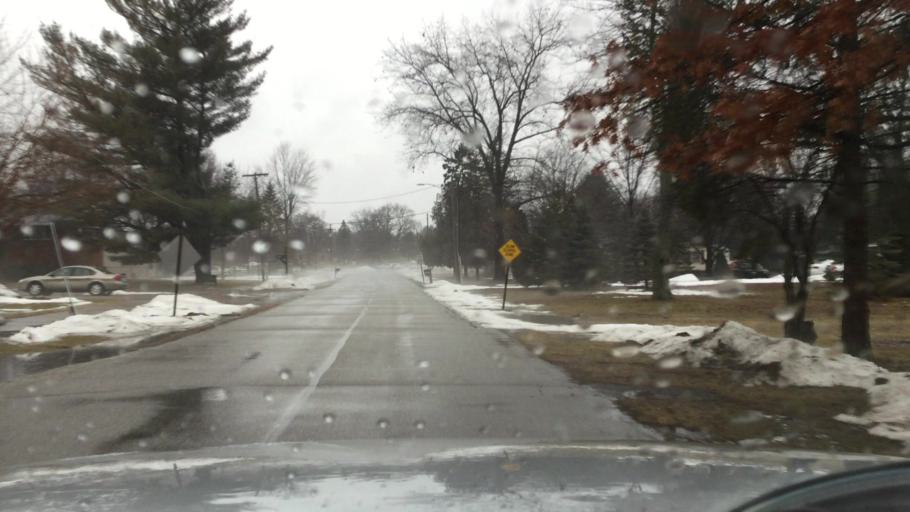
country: US
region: Michigan
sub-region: Saginaw County
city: Saint Charles
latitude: 43.2991
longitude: -84.1482
